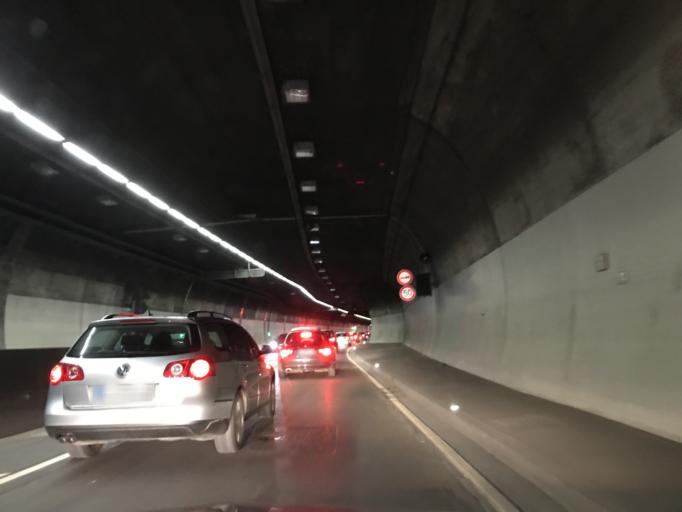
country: DE
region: Baden-Wuerttemberg
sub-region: Regierungsbezirk Stuttgart
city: Stuttgart
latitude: 48.7545
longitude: 9.1458
